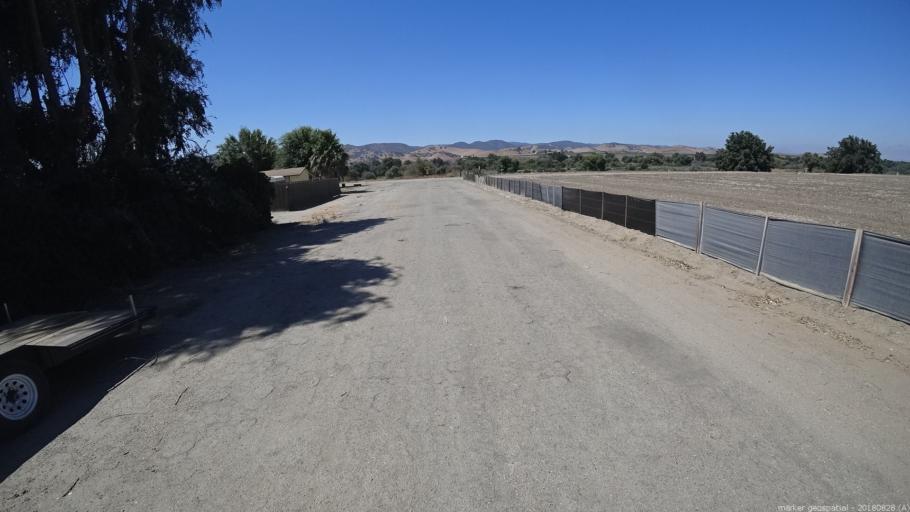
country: US
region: California
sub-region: Monterey County
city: King City
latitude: 36.0203
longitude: -120.9086
